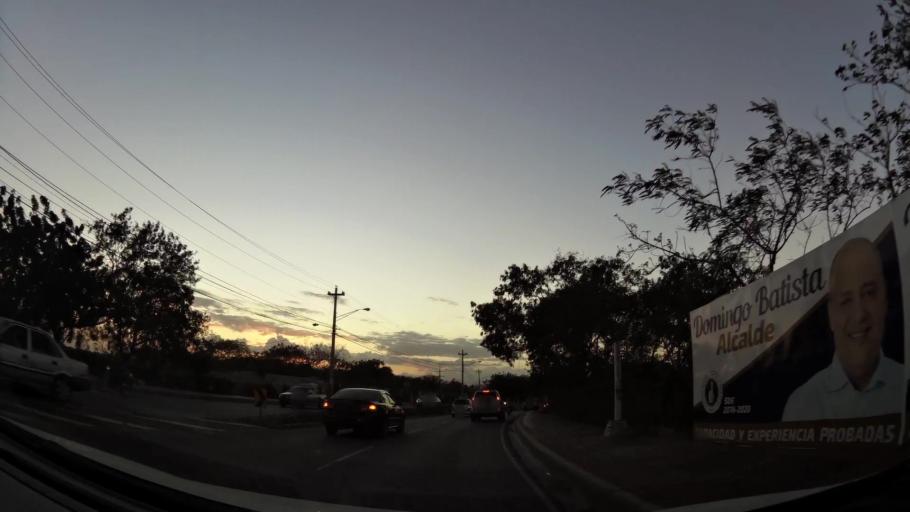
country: DO
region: Santo Domingo
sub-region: Santo Domingo
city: Santo Domingo Este
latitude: 18.4844
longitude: -69.8433
